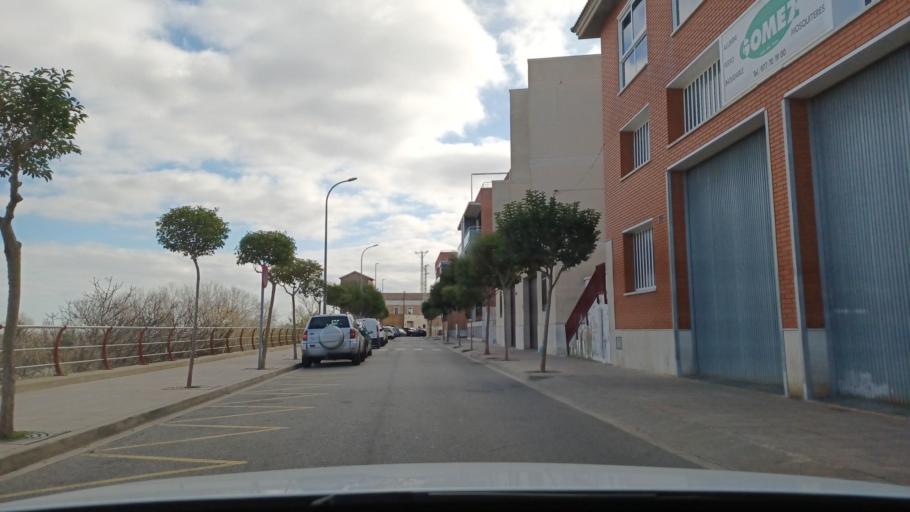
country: ES
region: Catalonia
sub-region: Provincia de Tarragona
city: Amposta
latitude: 40.7154
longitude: 0.5771
